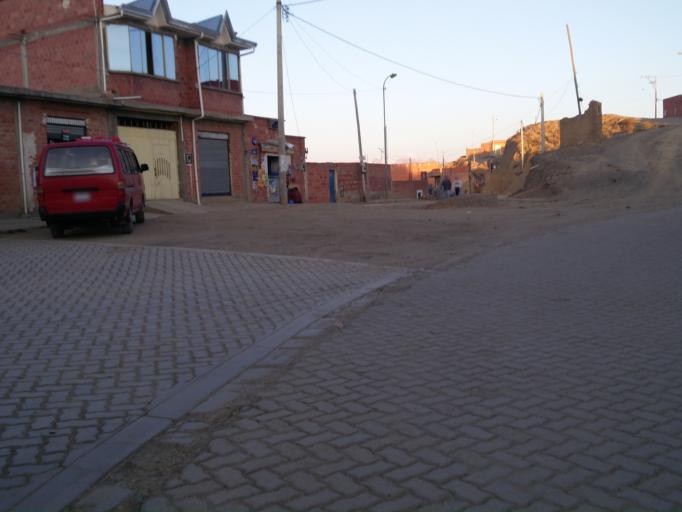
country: BO
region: La Paz
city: La Paz
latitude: -16.4795
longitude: -68.1651
